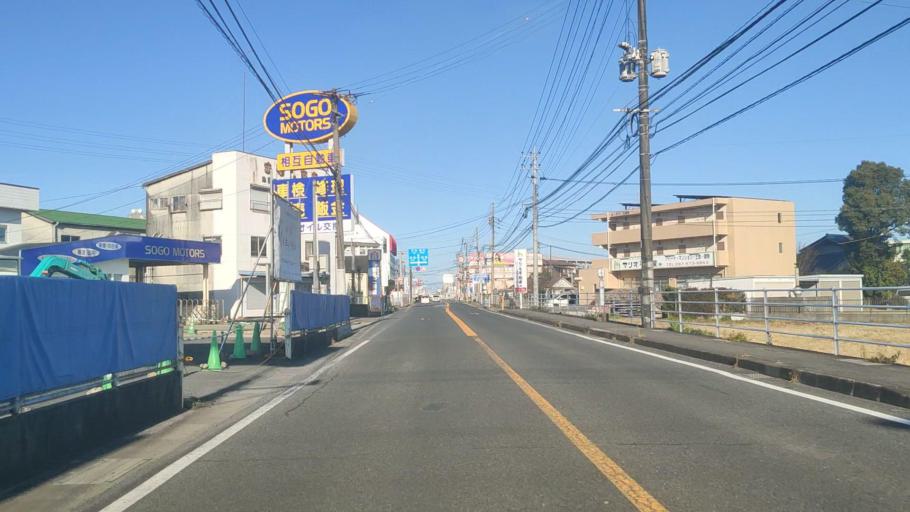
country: JP
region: Oita
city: Oita
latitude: 33.2154
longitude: 131.6117
